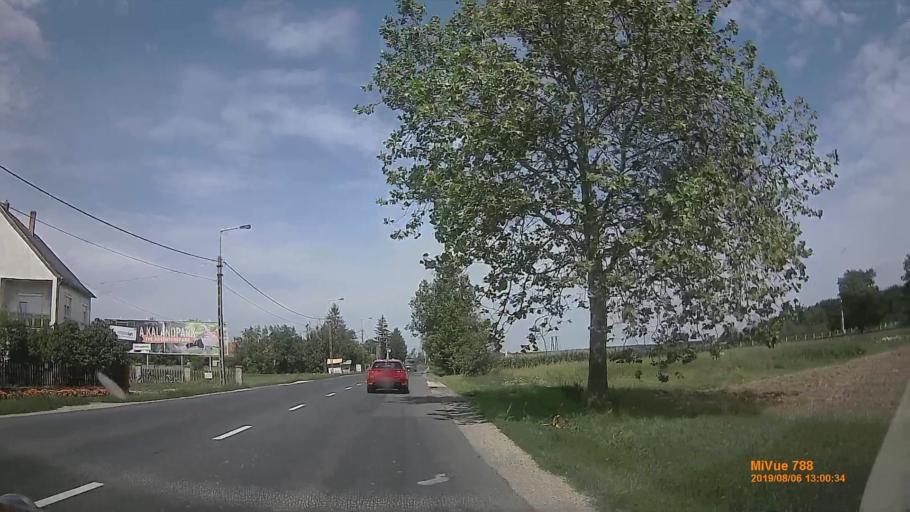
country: HU
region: Vas
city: Gencsapati
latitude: 47.3202
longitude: 16.5866
